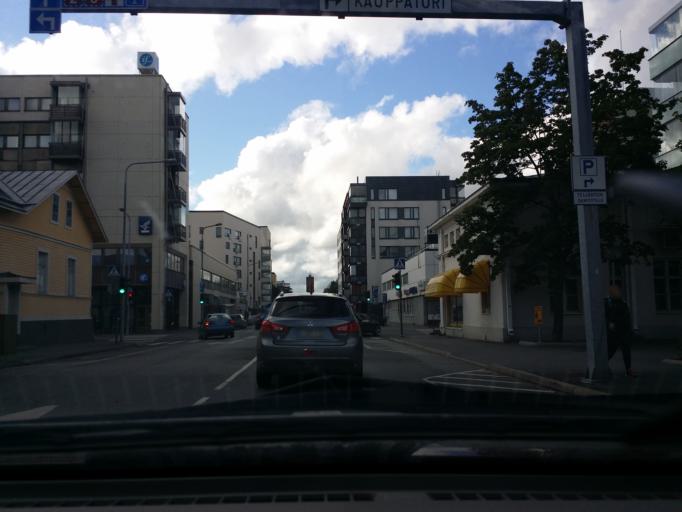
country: FI
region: Satakunta
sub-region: Pori
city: Pori
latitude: 61.4832
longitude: 21.7951
